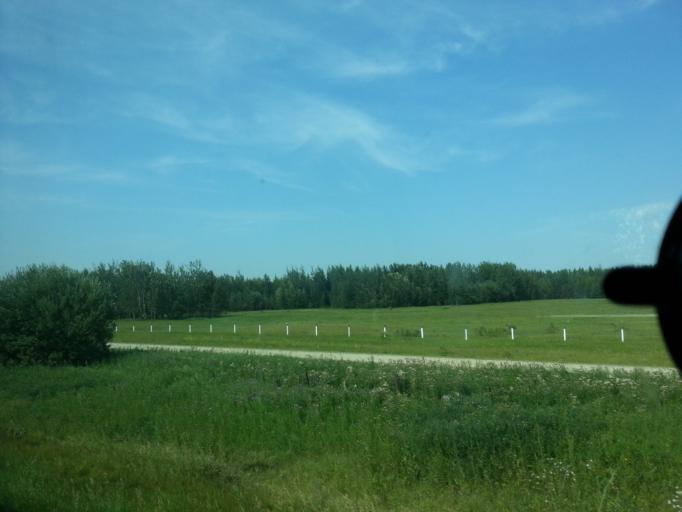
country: CA
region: Alberta
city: Mayerthorpe
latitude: 53.6102
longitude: -115.2067
